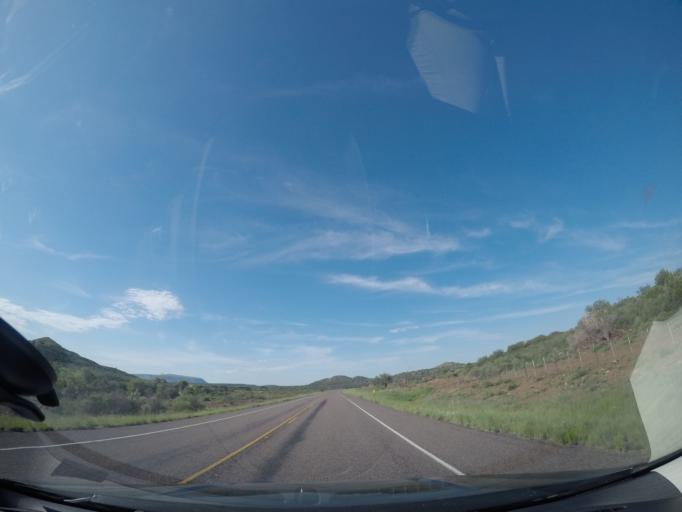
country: US
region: Texas
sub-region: Brewster County
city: Alpine
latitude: 30.1303
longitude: -103.5783
